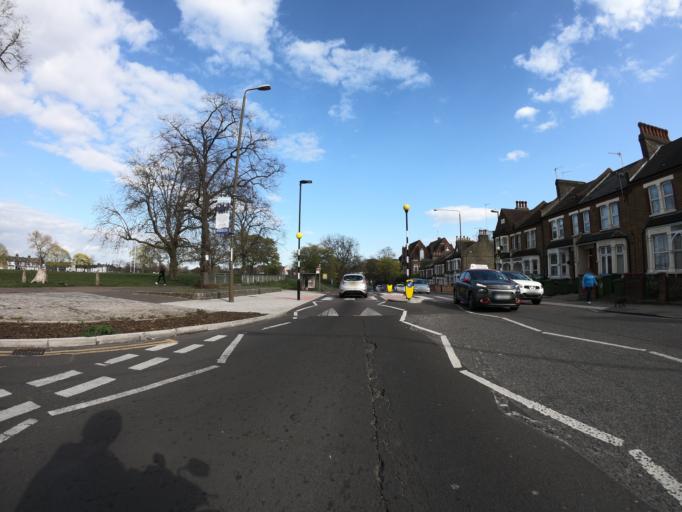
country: GB
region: England
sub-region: Greater London
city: Woolwich
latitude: 51.4801
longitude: 0.0849
